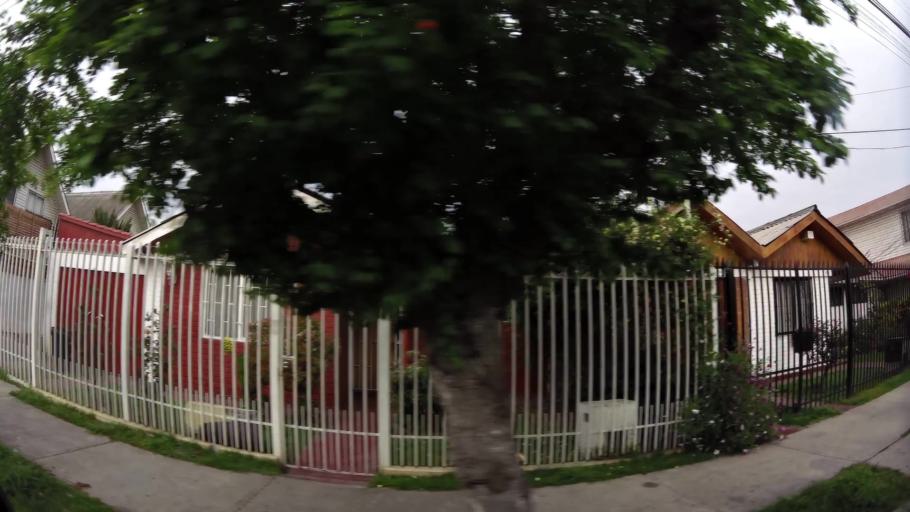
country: CL
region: Santiago Metropolitan
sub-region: Provincia de Santiago
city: Lo Prado
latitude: -33.5204
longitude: -70.7693
